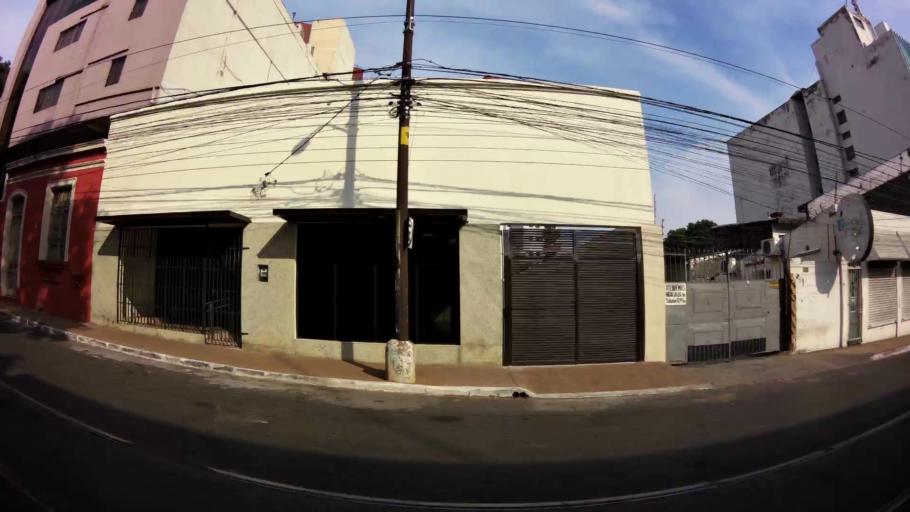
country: PY
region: Asuncion
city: Asuncion
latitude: -25.2854
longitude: -57.6250
